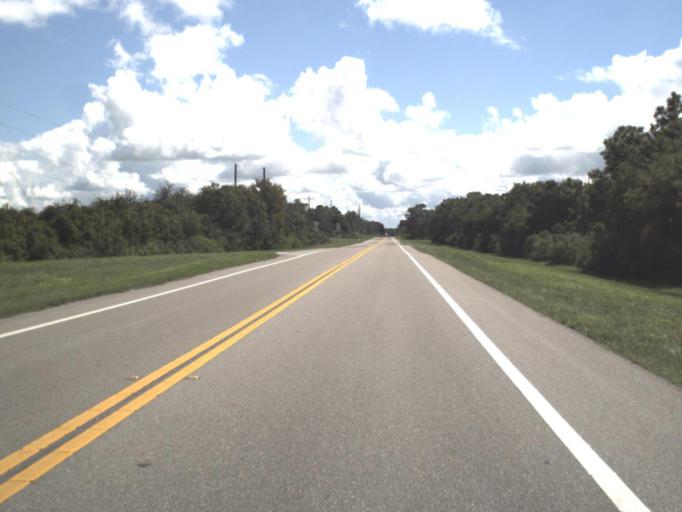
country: US
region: Florida
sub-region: Sarasota County
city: Fruitville
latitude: 27.3980
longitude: -82.3023
